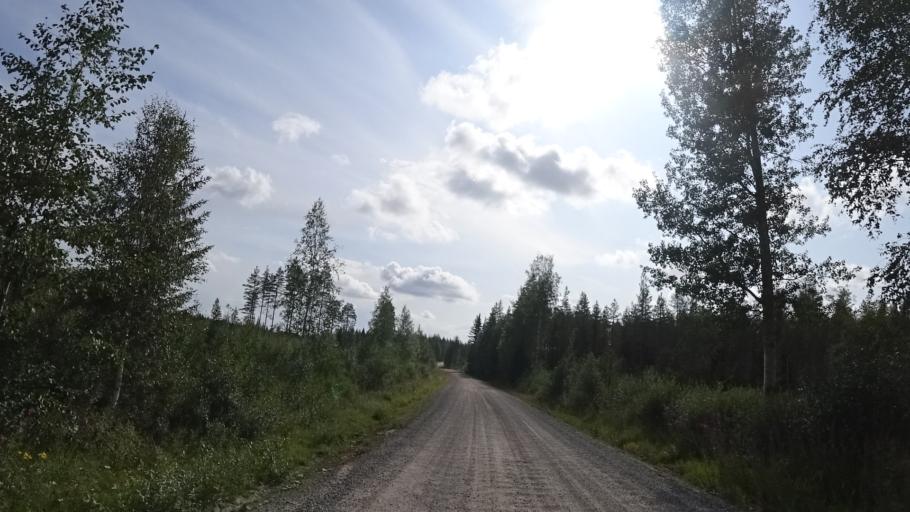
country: FI
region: North Karelia
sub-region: Pielisen Karjala
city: Lieksa
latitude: 63.5798
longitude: 30.1279
